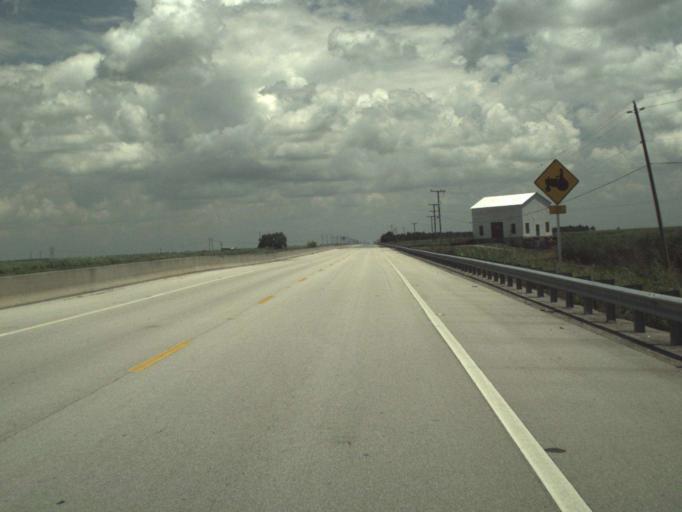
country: US
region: Florida
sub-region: Palm Beach County
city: Pahokee
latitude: 26.8432
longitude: -80.6035
